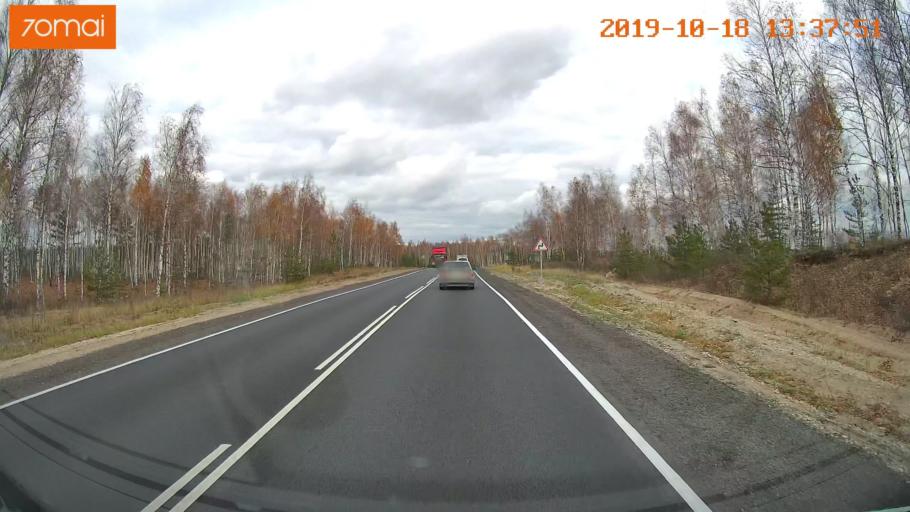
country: RU
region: Rjazan
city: Solotcha
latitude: 54.8834
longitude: 39.9993
